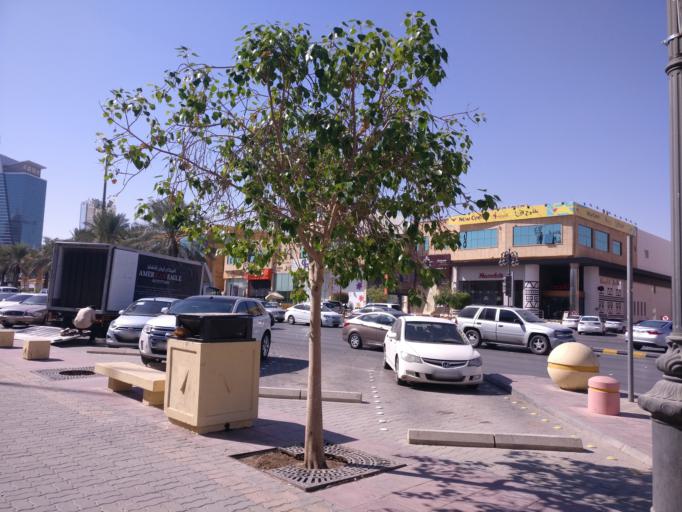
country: SA
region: Ar Riyad
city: Riyadh
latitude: 24.6990
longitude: 46.6902
